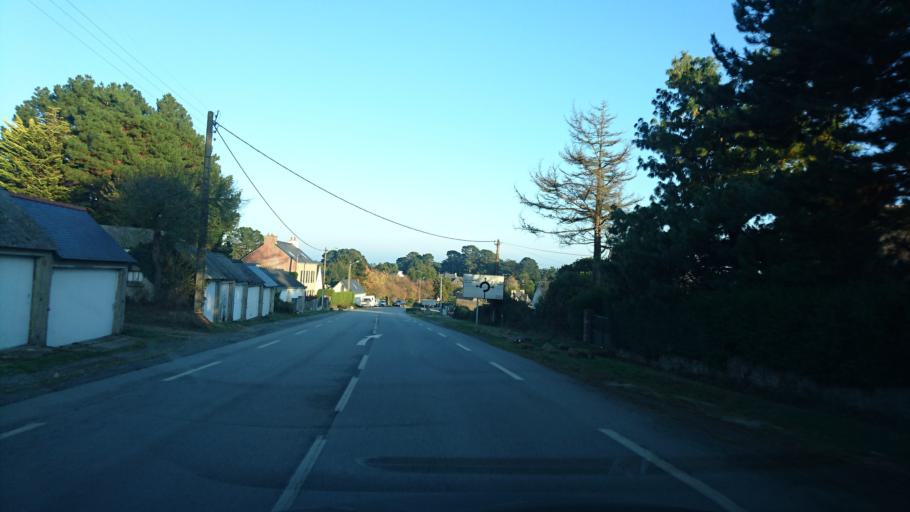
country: FR
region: Brittany
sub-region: Departement du Morbihan
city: Larmor-Baden
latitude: 47.6025
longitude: -2.8650
